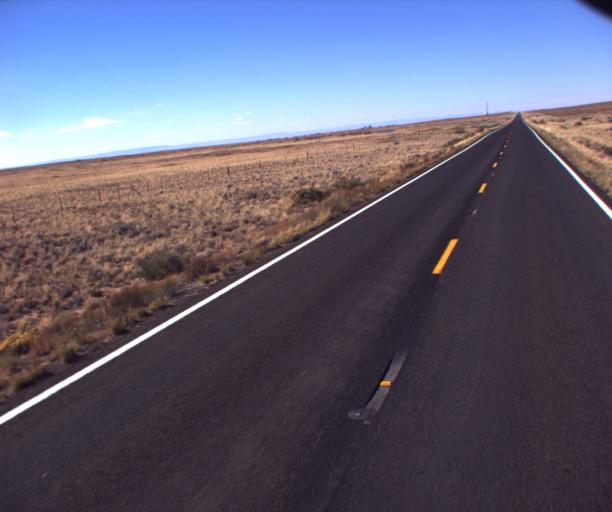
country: US
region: Arizona
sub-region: Coconino County
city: Tuba City
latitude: 35.9838
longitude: -110.9956
